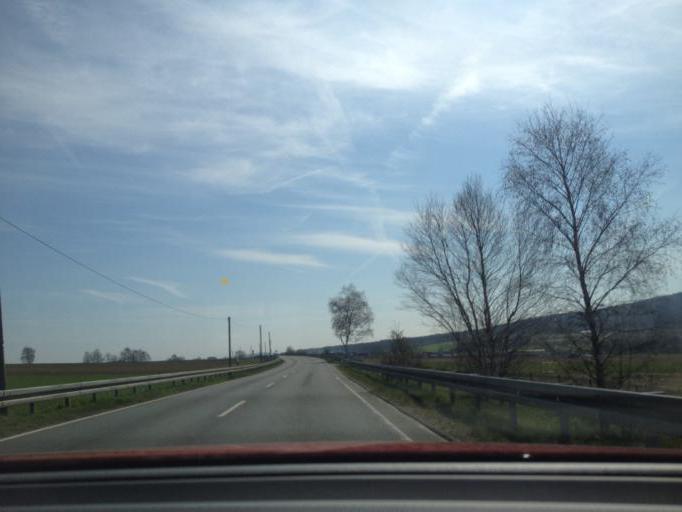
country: DE
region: Bavaria
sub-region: Upper Franconia
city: Zell im Fichtelgebirge
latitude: 50.0961
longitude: 11.8350
